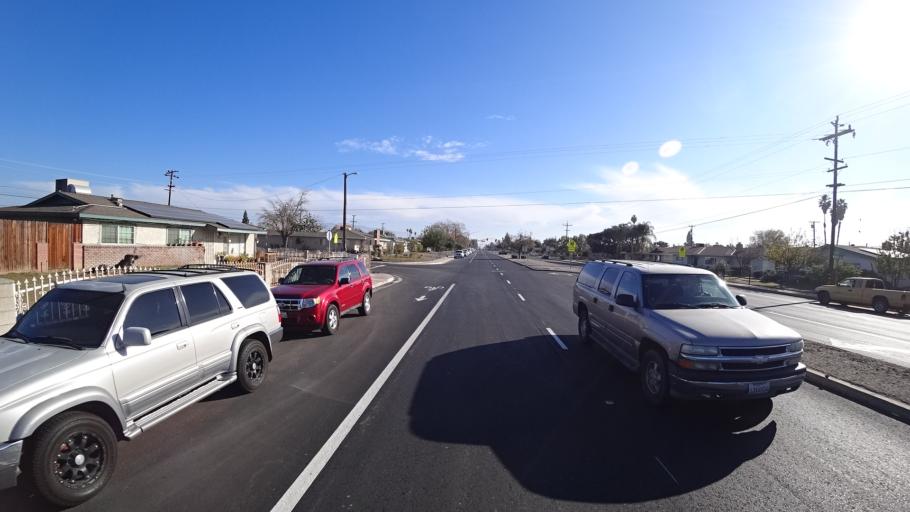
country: US
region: California
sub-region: Kern County
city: Greenfield
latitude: 35.3177
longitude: -119.0167
